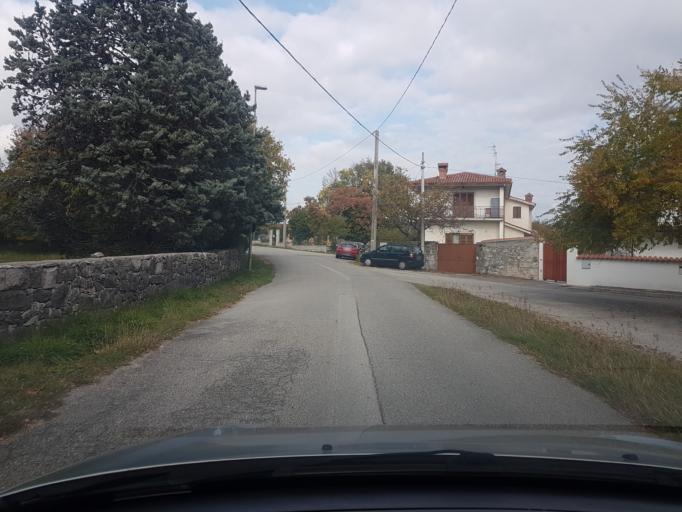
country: IT
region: Friuli Venezia Giulia
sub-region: Provincia di Trieste
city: Aurisina
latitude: 45.7520
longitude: 13.6707
